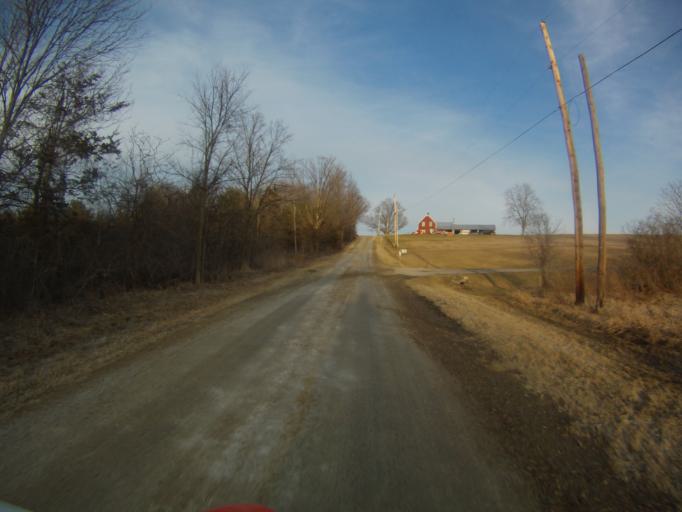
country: US
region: New York
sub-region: Essex County
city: Port Henry
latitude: 44.1180
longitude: -73.3723
